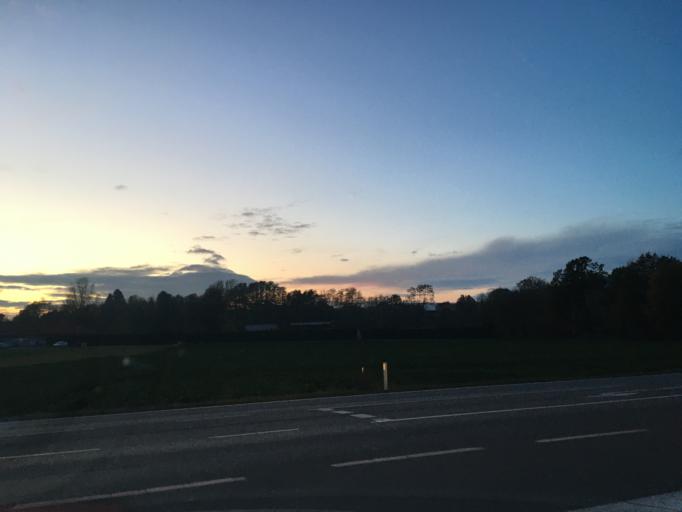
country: AT
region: Vienna
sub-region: Wien Stadt
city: Vienna
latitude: 48.2118
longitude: 16.3047
